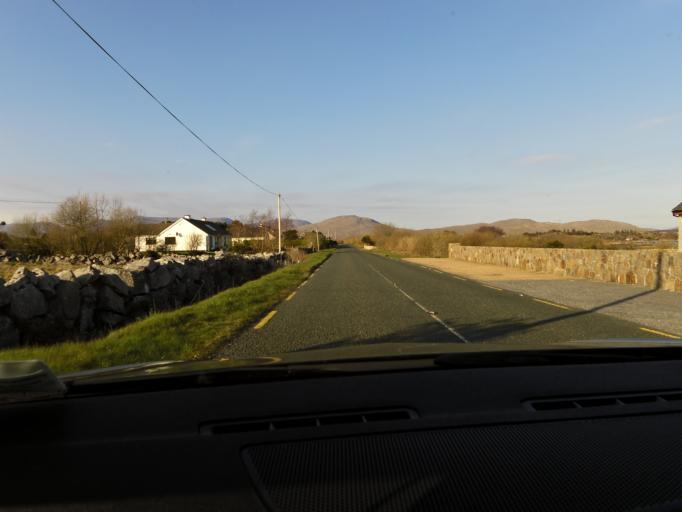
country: IE
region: Connaught
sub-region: County Galway
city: Oughterard
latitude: 53.3839
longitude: -9.6635
